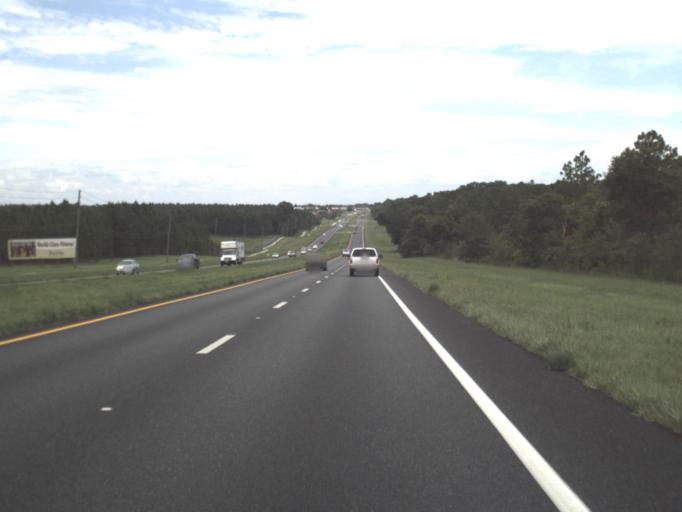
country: US
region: Florida
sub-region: Citrus County
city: Inverness Highlands North
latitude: 28.8564
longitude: -82.4094
